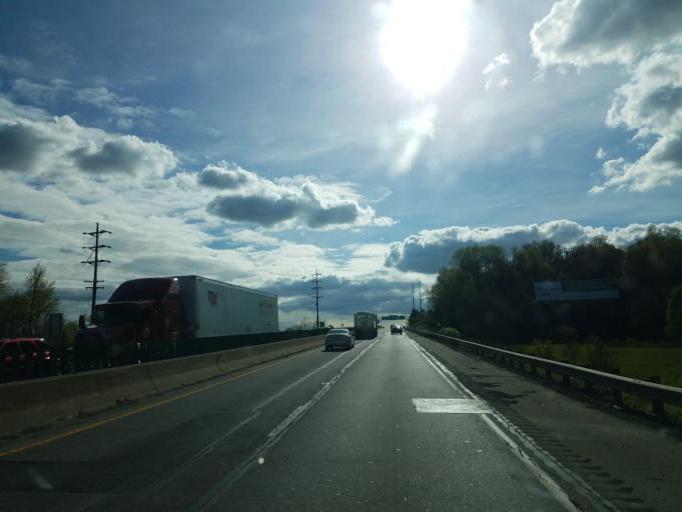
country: US
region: Ohio
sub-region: Richland County
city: Mansfield
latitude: 40.7774
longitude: -82.5283
